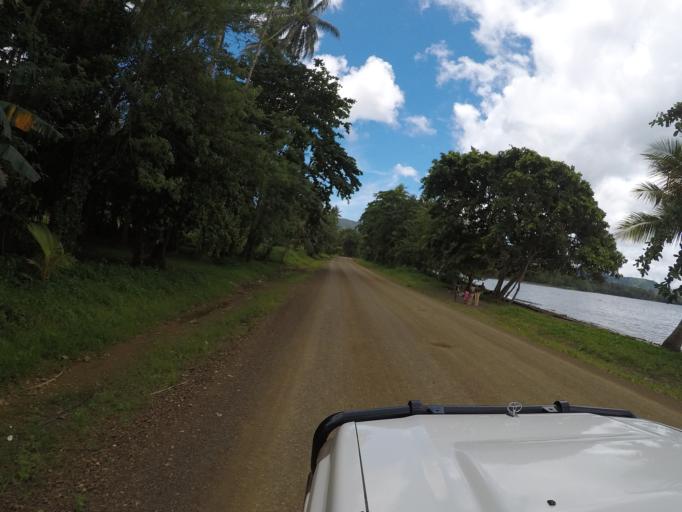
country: PG
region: Milne Bay
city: Alotau
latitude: -10.3365
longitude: 150.6479
